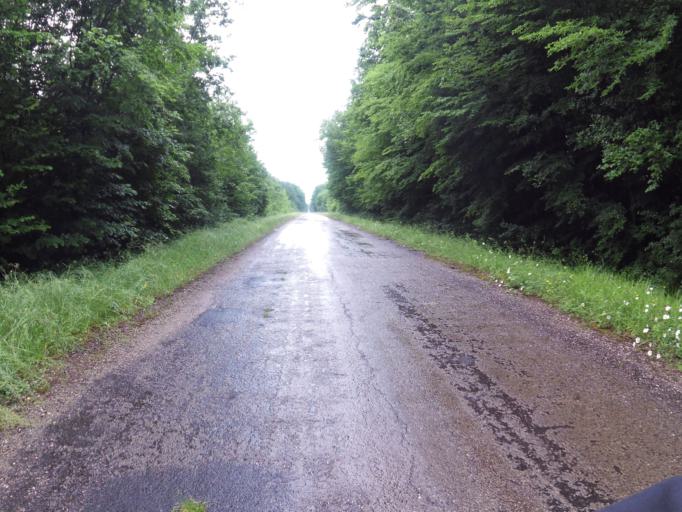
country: FR
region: Champagne-Ardenne
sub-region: Departement de la Marne
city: Sermaize-les-Bains
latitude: 48.7546
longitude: 4.9572
